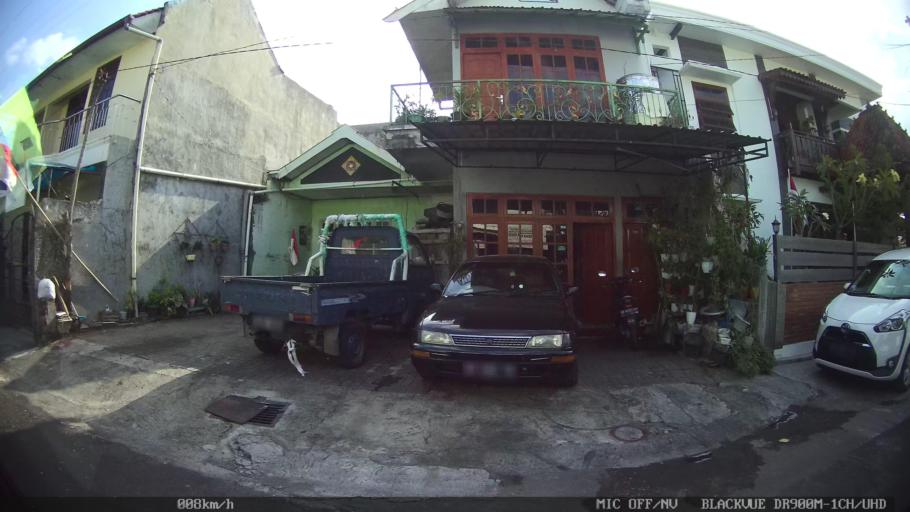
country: ID
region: Daerah Istimewa Yogyakarta
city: Yogyakarta
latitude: -7.7922
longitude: 110.3525
